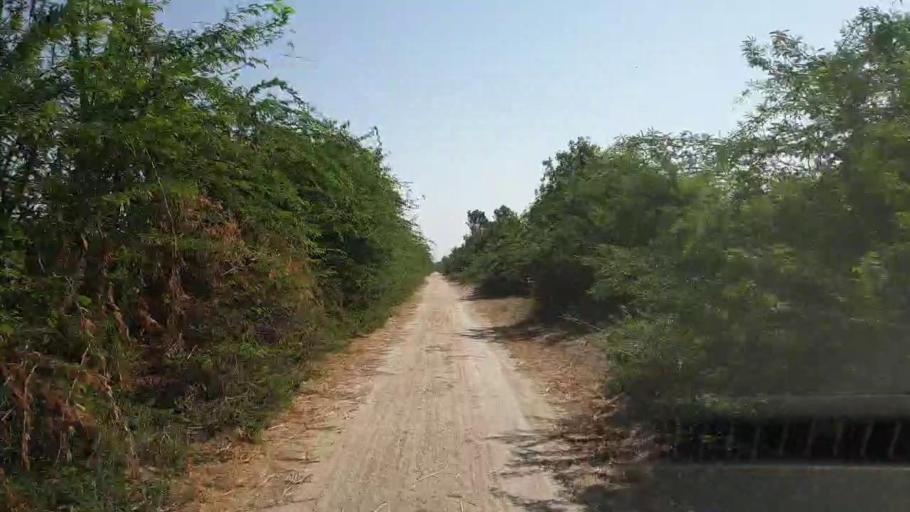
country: PK
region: Sindh
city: Tando Bago
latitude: 24.6552
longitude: 68.9809
